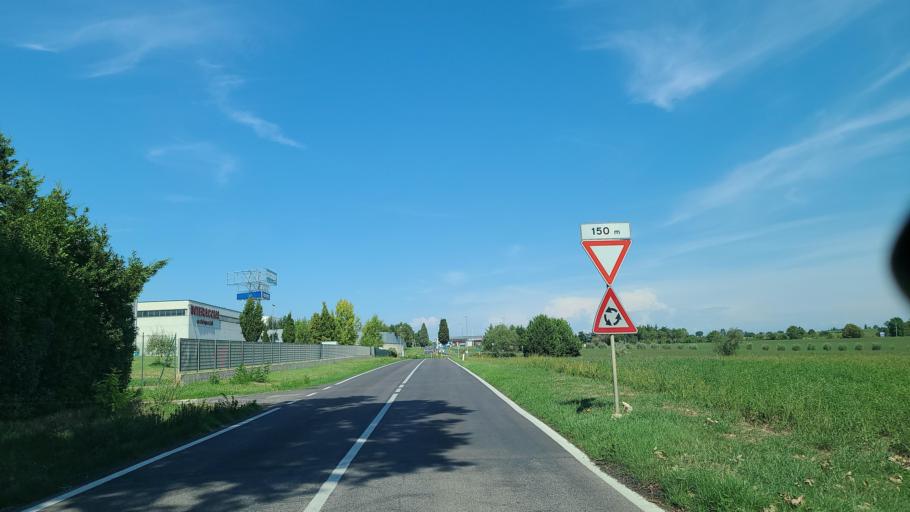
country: IT
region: Tuscany
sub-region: Provincia di Siena
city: Staggia
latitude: 43.4055
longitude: 11.1686
